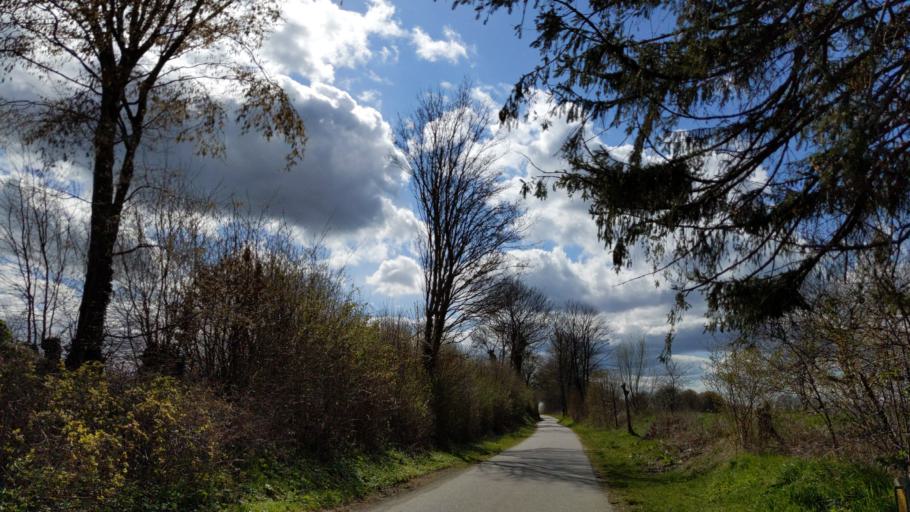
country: DE
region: Mecklenburg-Vorpommern
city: Selmsdorf
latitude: 53.8848
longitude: 10.8891
